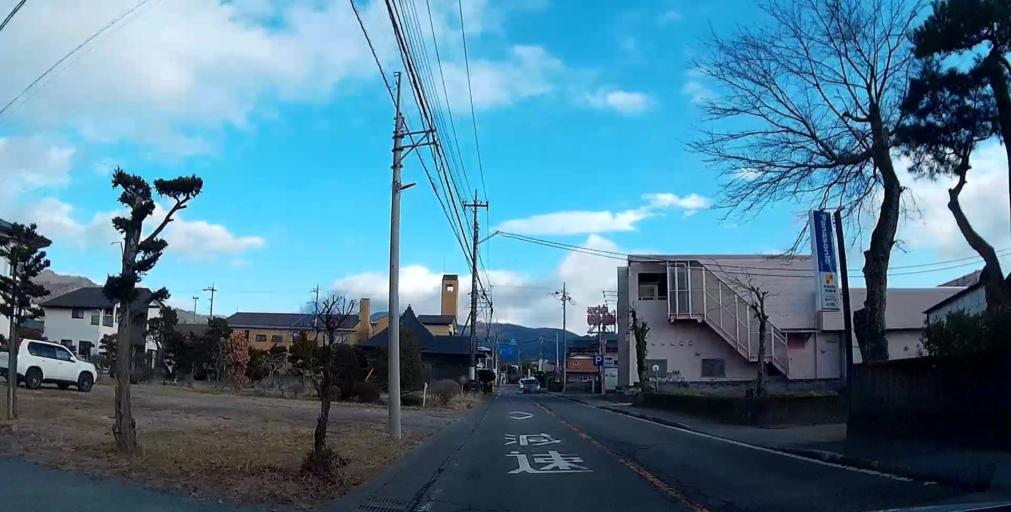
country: JP
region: Yamanashi
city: Otsuki
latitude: 35.4579
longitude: 138.8567
